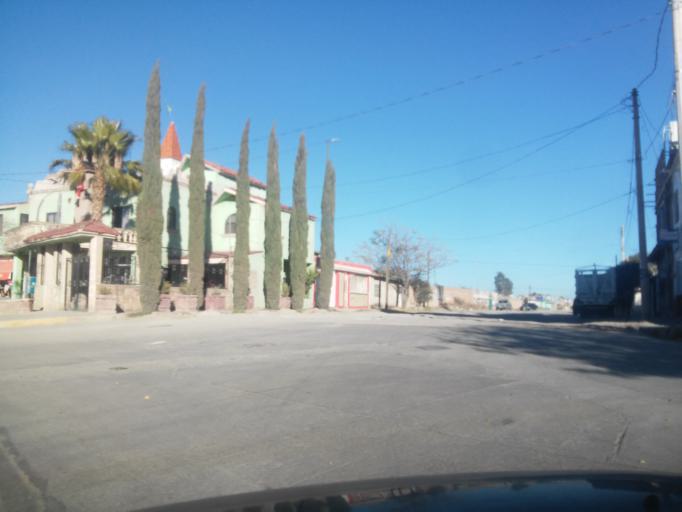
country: MX
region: Durango
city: Victoria de Durango
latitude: 24.0157
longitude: -104.6381
